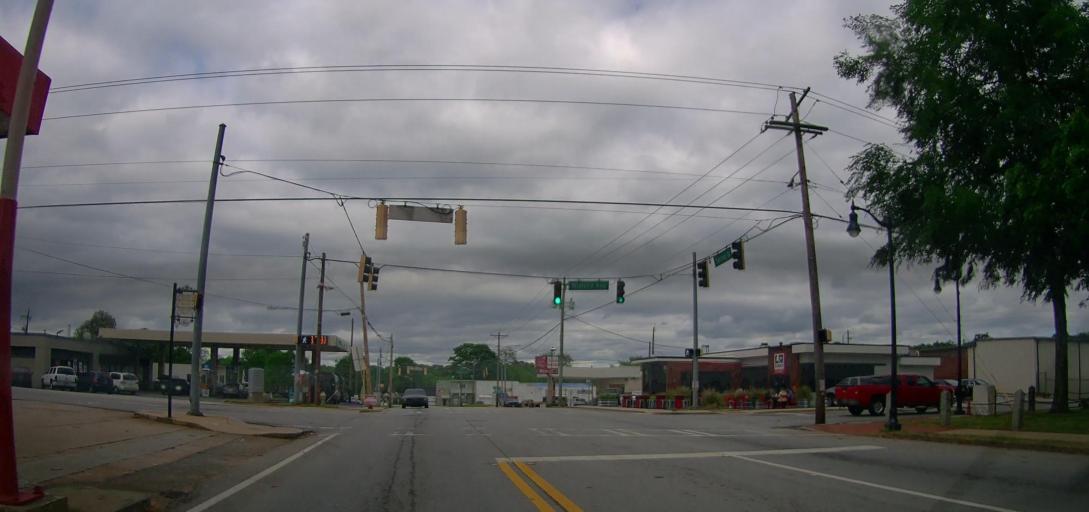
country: US
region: Georgia
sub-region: Walton County
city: Monroe
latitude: 33.7950
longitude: -83.7118
